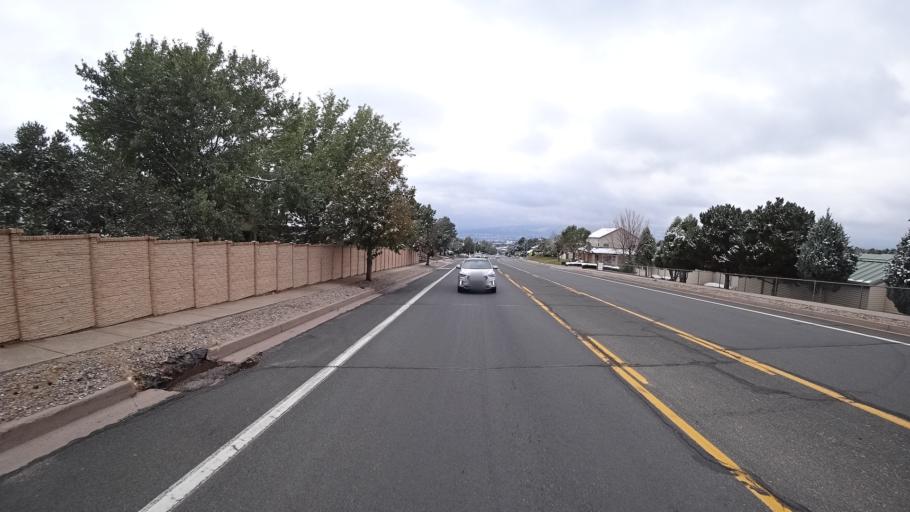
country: US
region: Colorado
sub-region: El Paso County
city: Cimarron Hills
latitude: 38.9161
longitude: -104.7619
